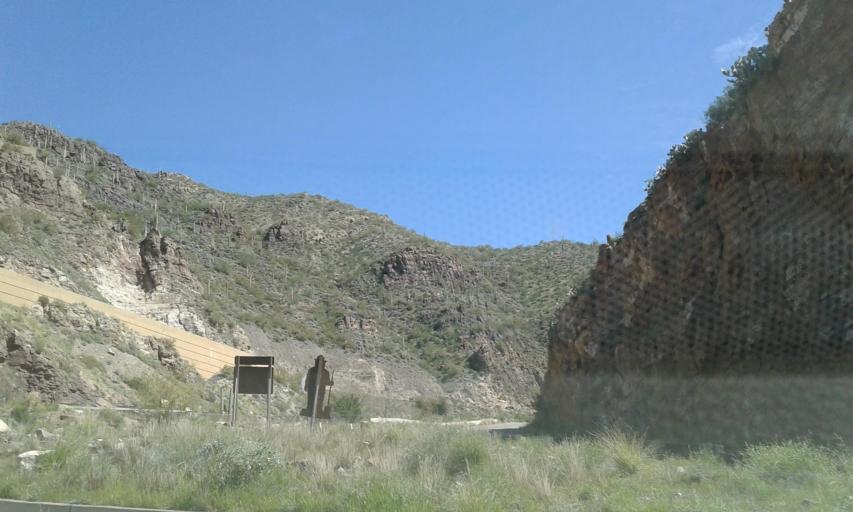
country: US
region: Arizona
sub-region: Gila County
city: Tonto Basin
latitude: 33.6683
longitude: -111.1621
